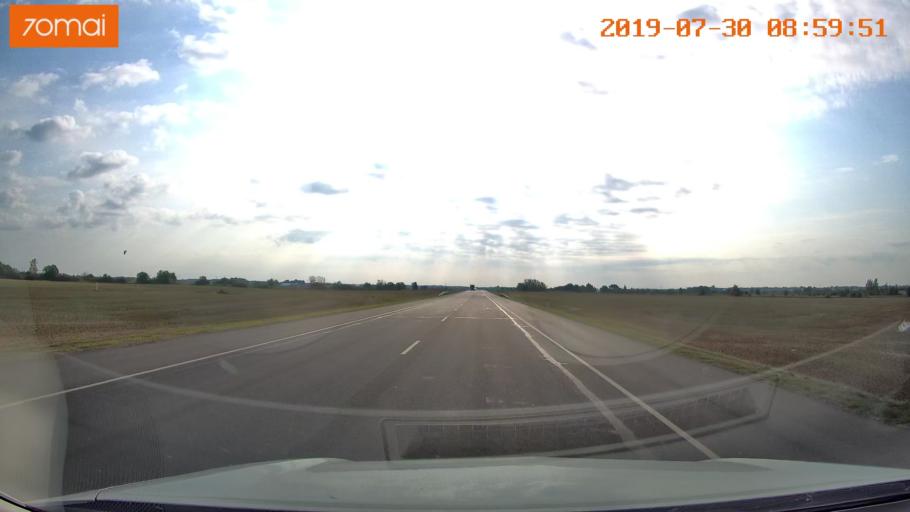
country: RU
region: Kaliningrad
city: Gusev
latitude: 54.6150
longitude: 22.1651
